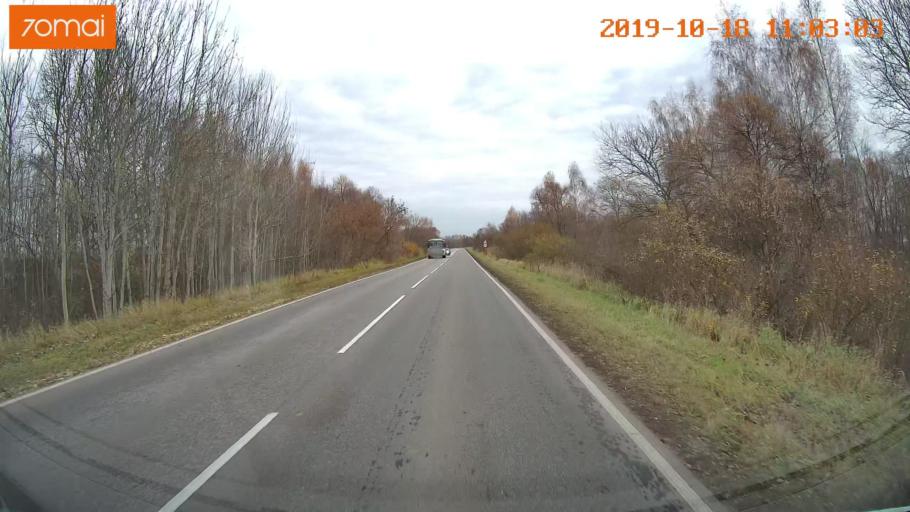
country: RU
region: Tula
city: Yepifan'
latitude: 53.8742
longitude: 38.5458
